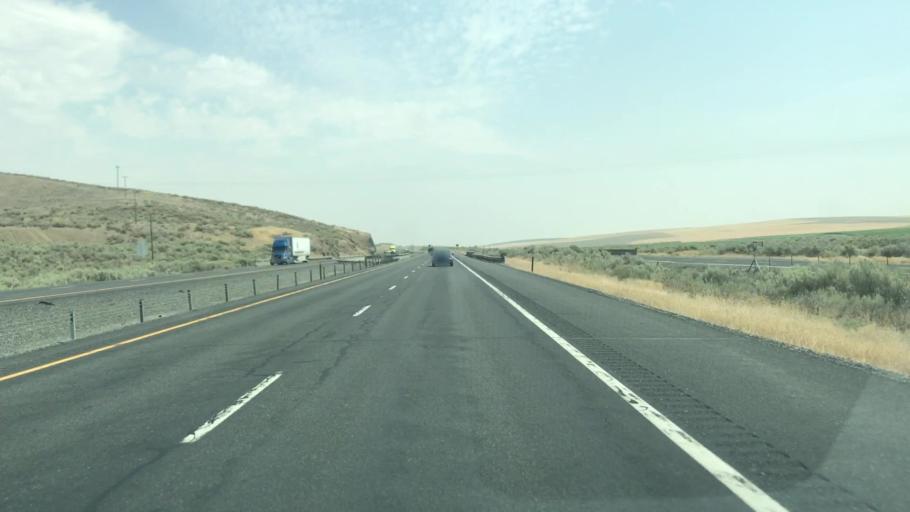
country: US
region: Washington
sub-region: Grant County
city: Warden
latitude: 47.0844
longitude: -118.9874
